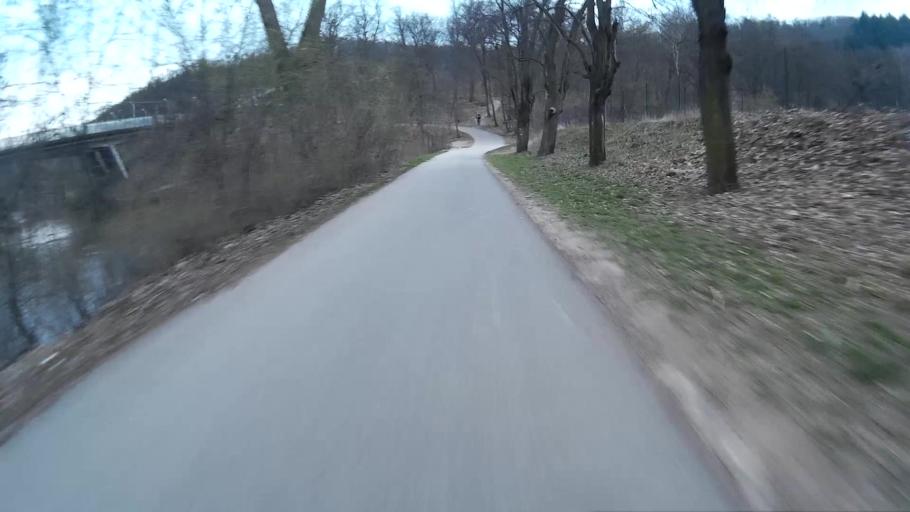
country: CZ
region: South Moravian
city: Ostopovice
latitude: 49.1893
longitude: 16.5665
